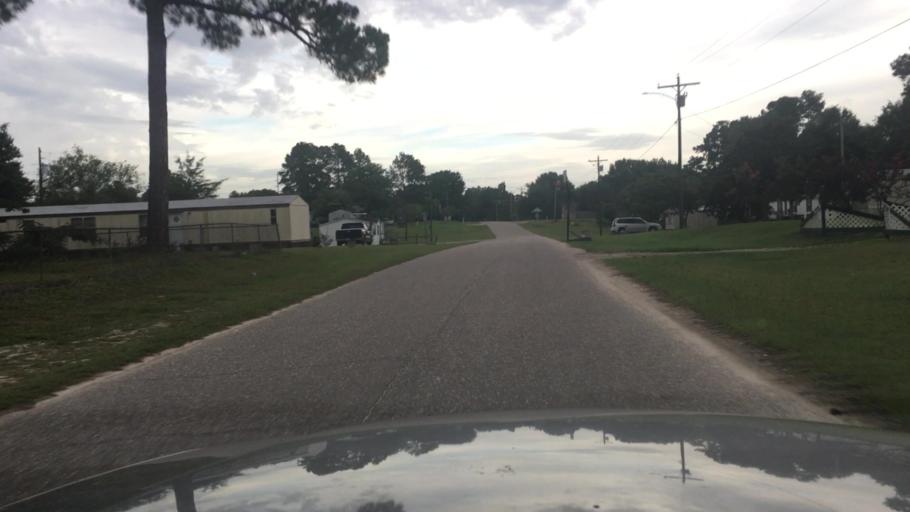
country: US
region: North Carolina
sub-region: Hoke County
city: Rockfish
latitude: 34.9847
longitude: -79.0344
